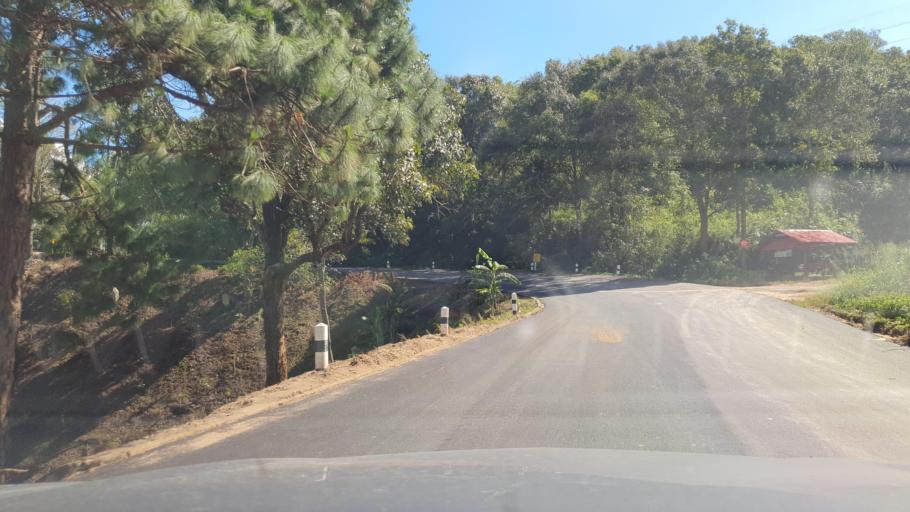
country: TH
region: Chiang Mai
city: Phrao
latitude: 19.3181
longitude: 99.3281
